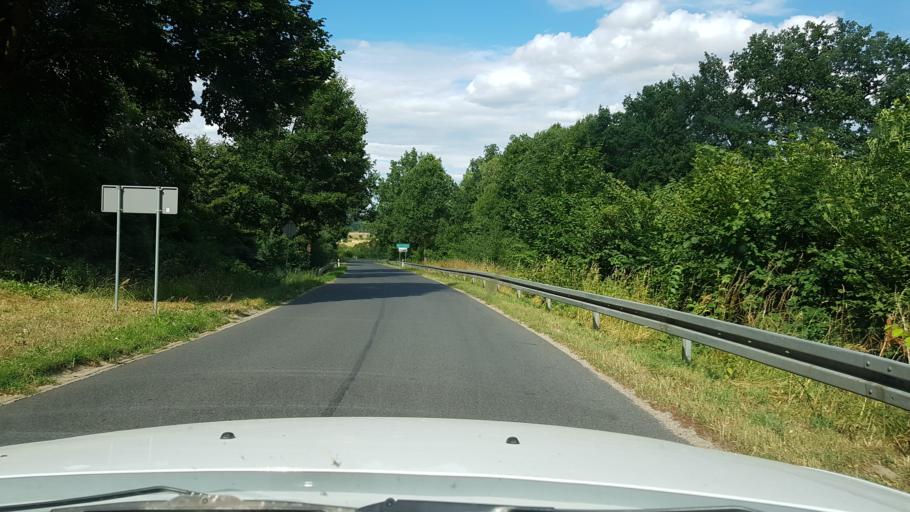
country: PL
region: West Pomeranian Voivodeship
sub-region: Powiat drawski
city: Kalisz Pomorski
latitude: 53.3938
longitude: 15.9578
